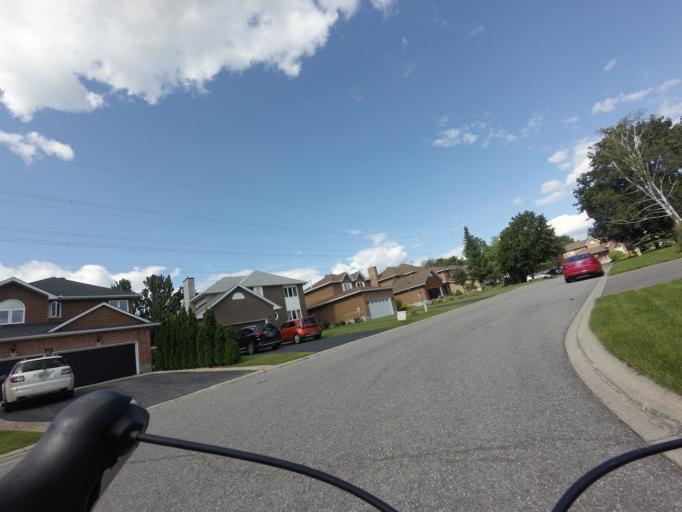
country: CA
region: Ontario
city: Bells Corners
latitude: 45.2875
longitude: -75.8525
